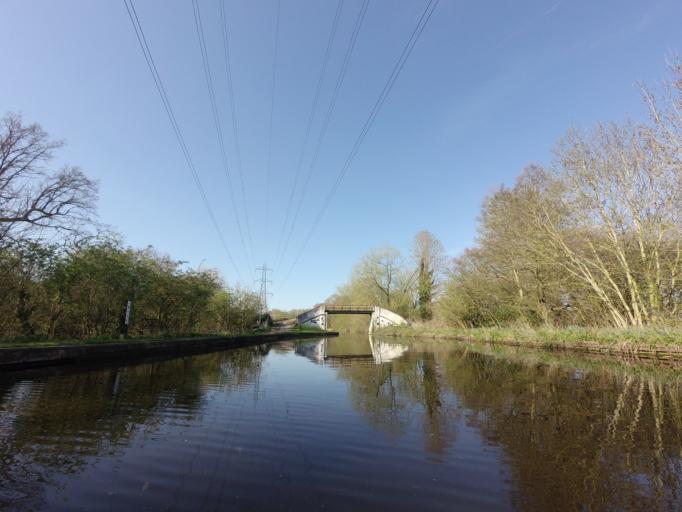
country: GB
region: England
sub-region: Buckinghamshire
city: Denham
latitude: 51.5689
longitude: -0.4818
